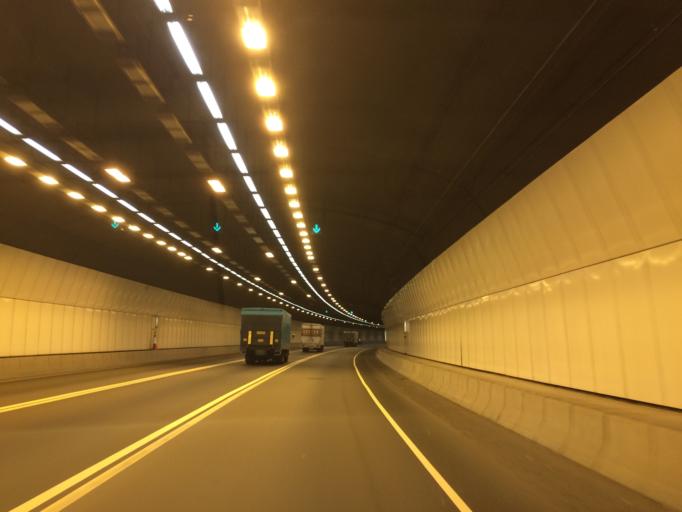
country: HK
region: Wong Tai Sin
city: Wong Tai Sin
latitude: 22.3616
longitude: 114.1636
